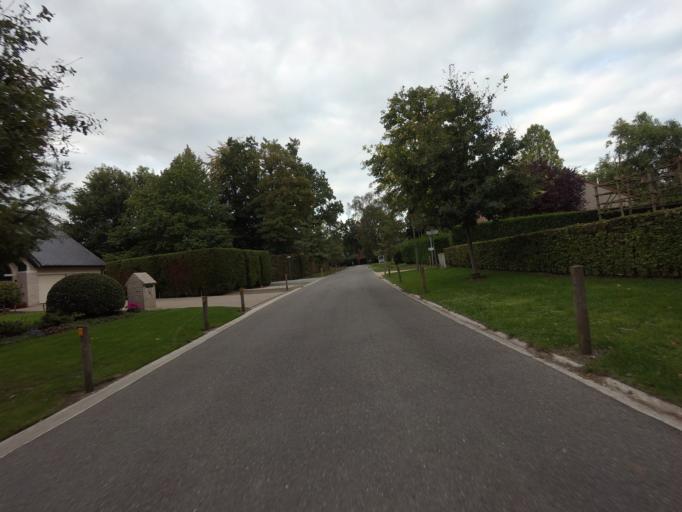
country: BE
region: Flanders
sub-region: Provincie Vlaams-Brabant
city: Kampenhout
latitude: 50.9345
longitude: 4.5554
